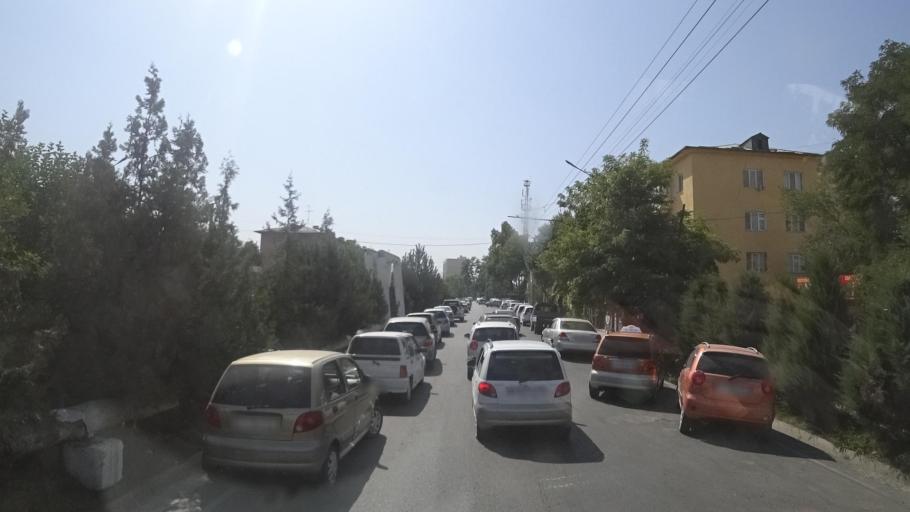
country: KG
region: Osh
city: Osh
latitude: 40.5193
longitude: 72.8100
